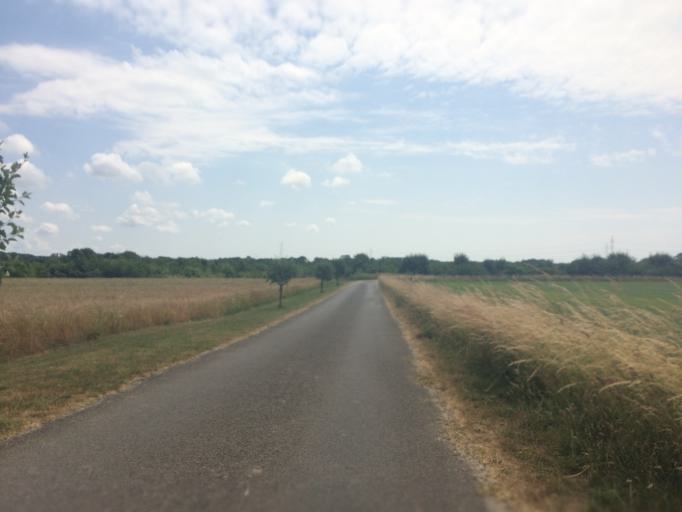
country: DK
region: Capital Region
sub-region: Bornholm Kommune
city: Ronne
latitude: 55.1730
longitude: 14.7262
